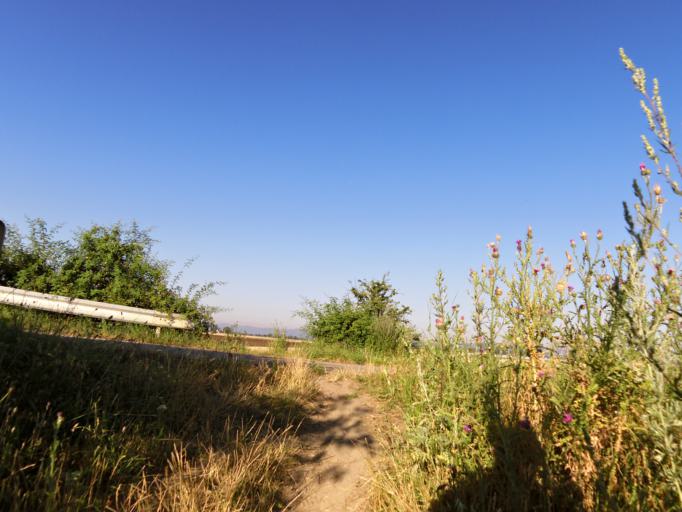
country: DE
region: Rheinland-Pfalz
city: Frankenthal
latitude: 49.4980
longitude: 8.3539
